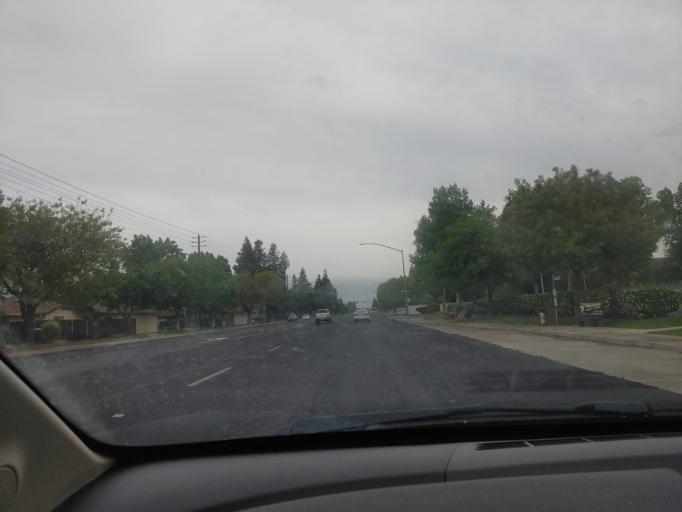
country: US
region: California
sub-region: Stanislaus County
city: Salida
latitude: 37.6938
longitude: -121.0499
